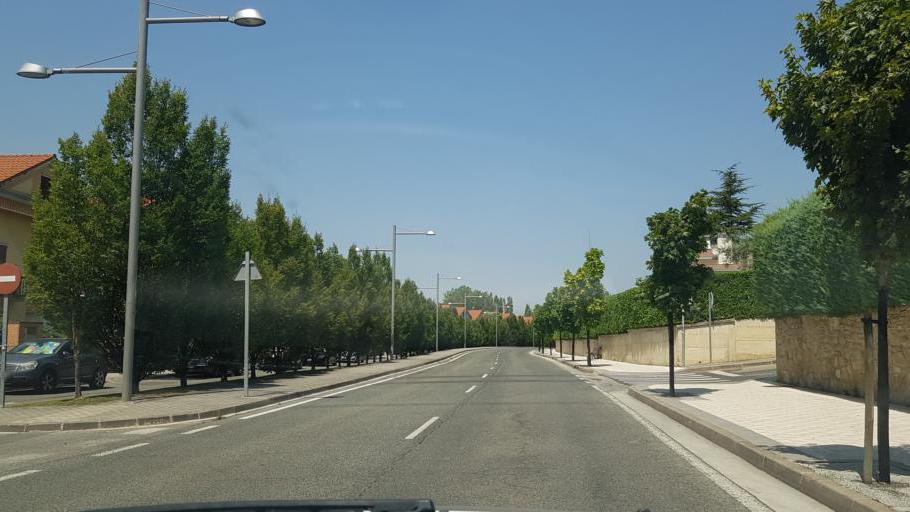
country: ES
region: Navarre
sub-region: Provincia de Navarra
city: Segundo Ensanche
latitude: 42.7932
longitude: -1.6203
